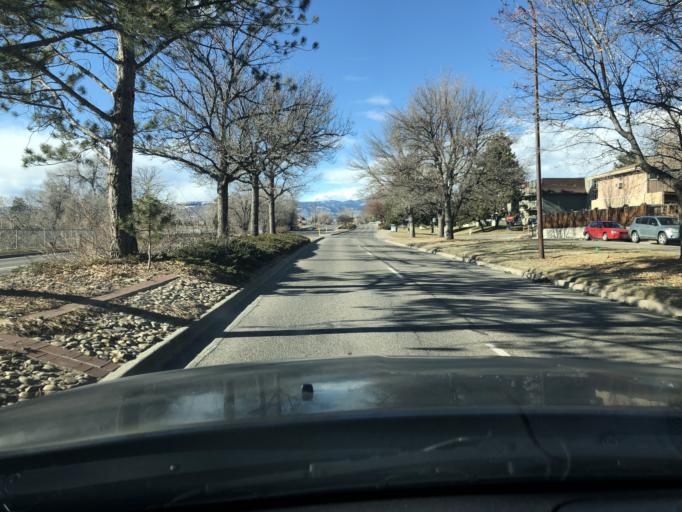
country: US
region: Colorado
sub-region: Jefferson County
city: Arvada
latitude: 39.8019
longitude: -105.1328
